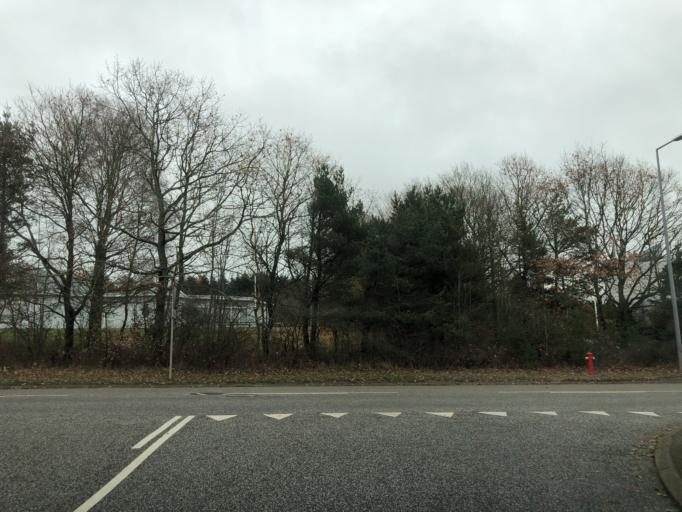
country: DK
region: Central Jutland
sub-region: Skanderborg Kommune
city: Ry
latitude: 56.0889
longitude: 9.7838
